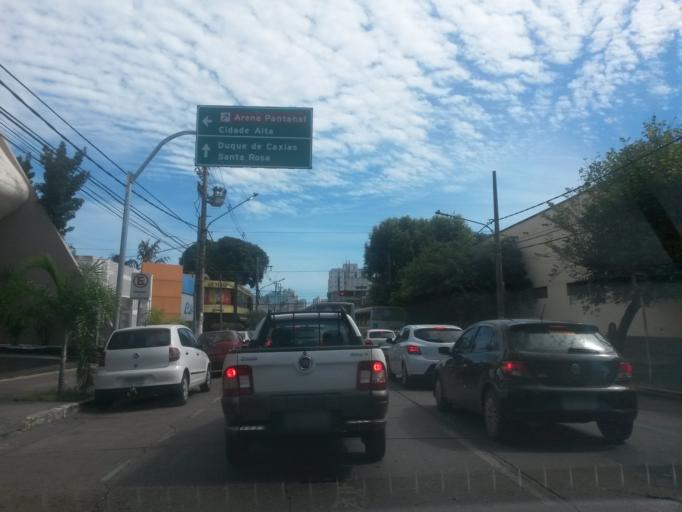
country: BR
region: Mato Grosso
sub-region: Cuiaba
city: Cuiaba
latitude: -15.5928
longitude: -56.1028
